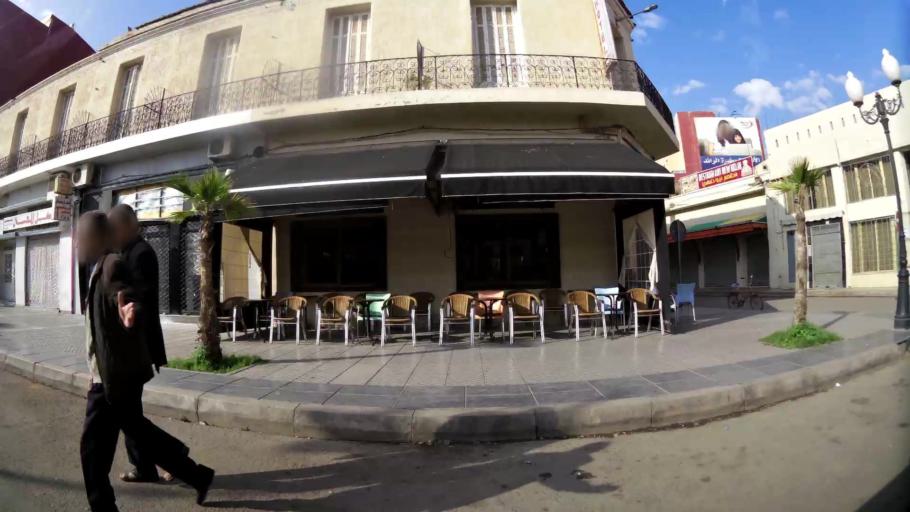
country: MA
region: Oriental
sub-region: Oujda-Angad
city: Oujda
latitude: 34.6827
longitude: -1.9154
